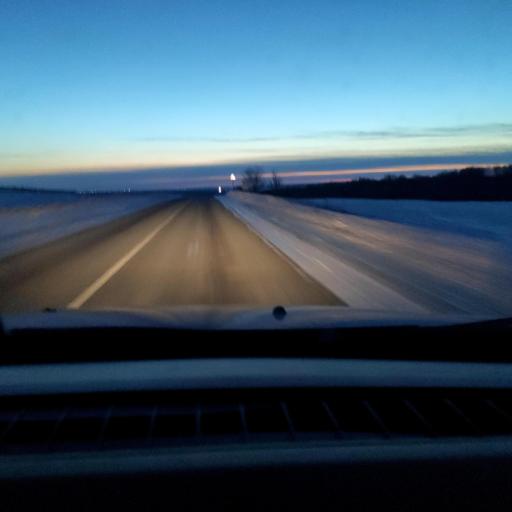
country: RU
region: Samara
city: Kinel'
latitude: 53.3035
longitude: 50.7965
